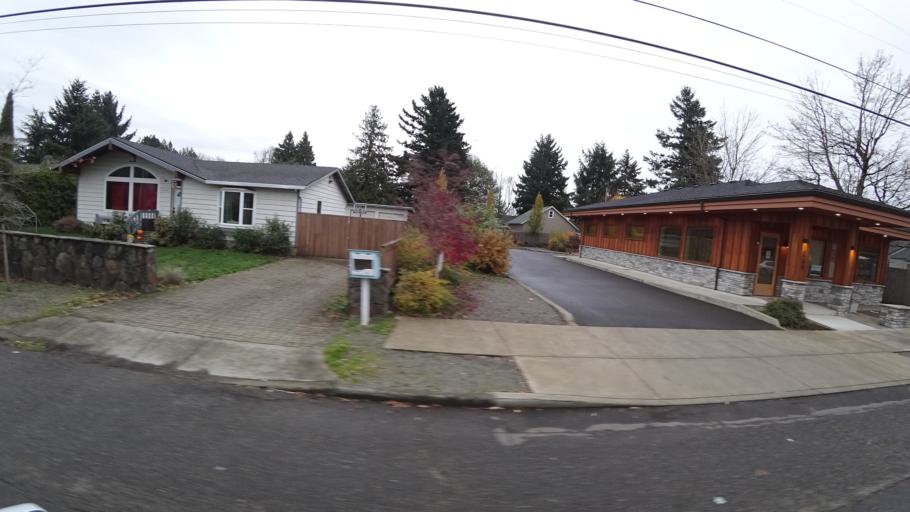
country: US
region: Oregon
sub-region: Multnomah County
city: Lents
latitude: 45.5299
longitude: -122.5570
